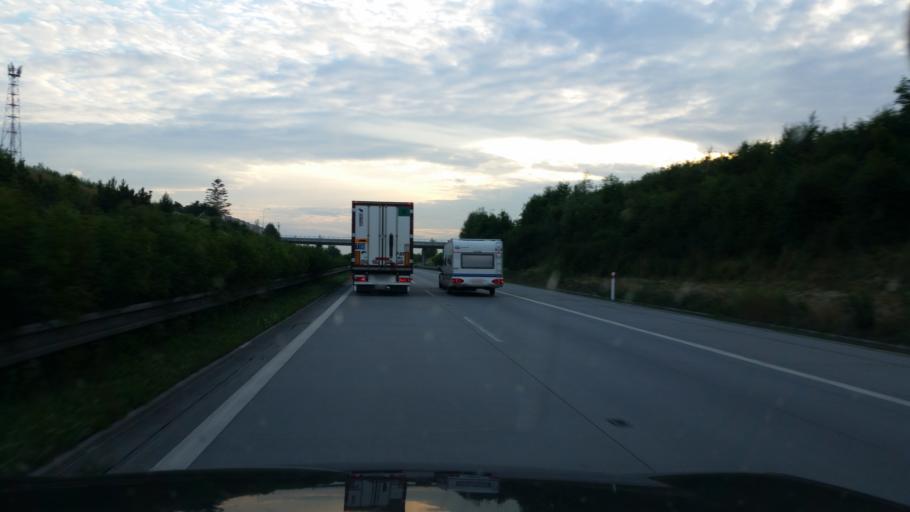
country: CZ
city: Klimkovice
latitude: 49.8006
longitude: 18.1636
